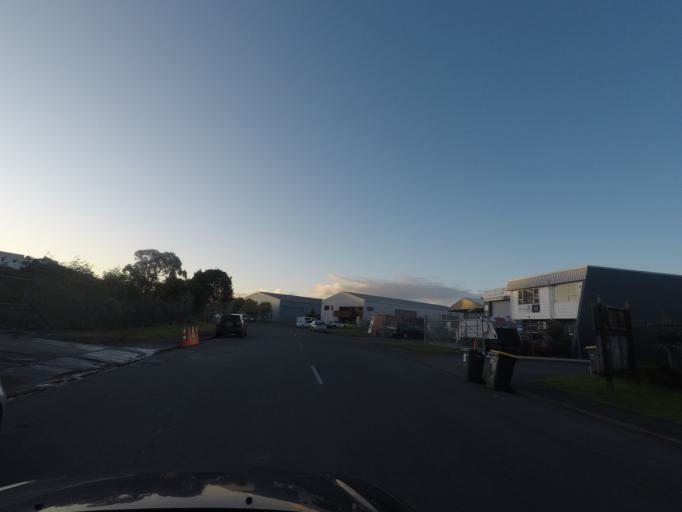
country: NZ
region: Auckland
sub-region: Auckland
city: Rosebank
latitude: -36.8906
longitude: 174.6592
